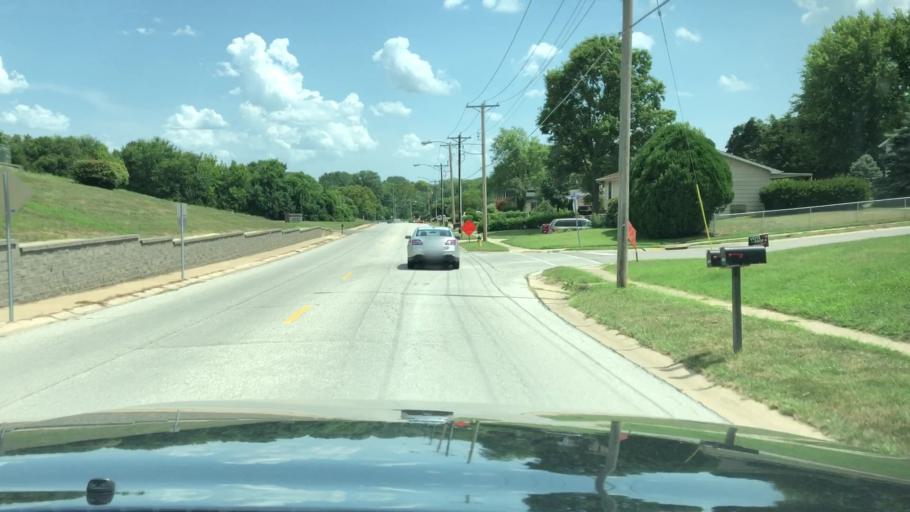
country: US
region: Missouri
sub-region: Saint Charles County
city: Saint Charles
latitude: 38.7996
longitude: -90.5299
